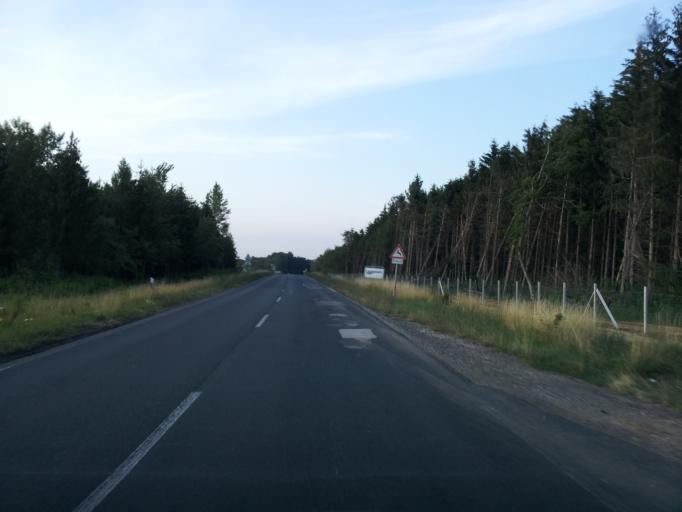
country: HU
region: Zala
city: Zalalovo
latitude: 46.8169
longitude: 16.5782
